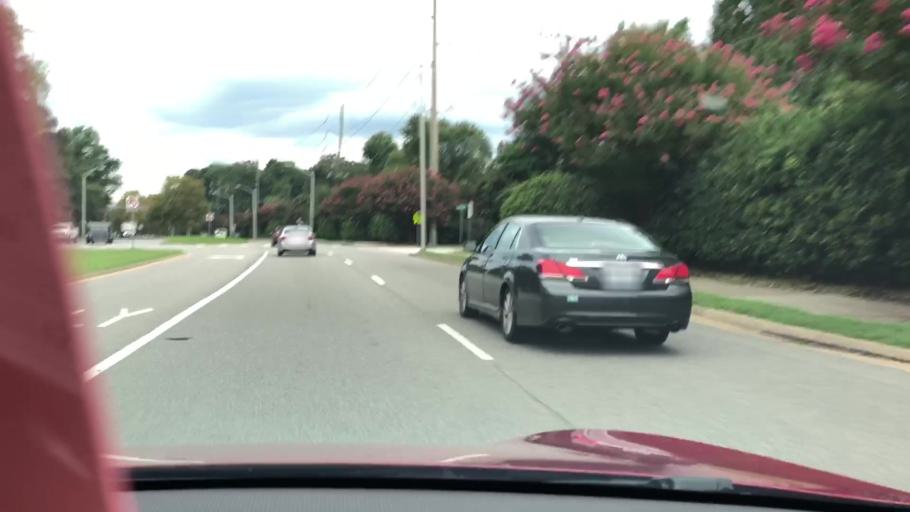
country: US
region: Virginia
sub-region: City of Virginia Beach
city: Virginia Beach
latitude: 36.8887
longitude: -76.0506
